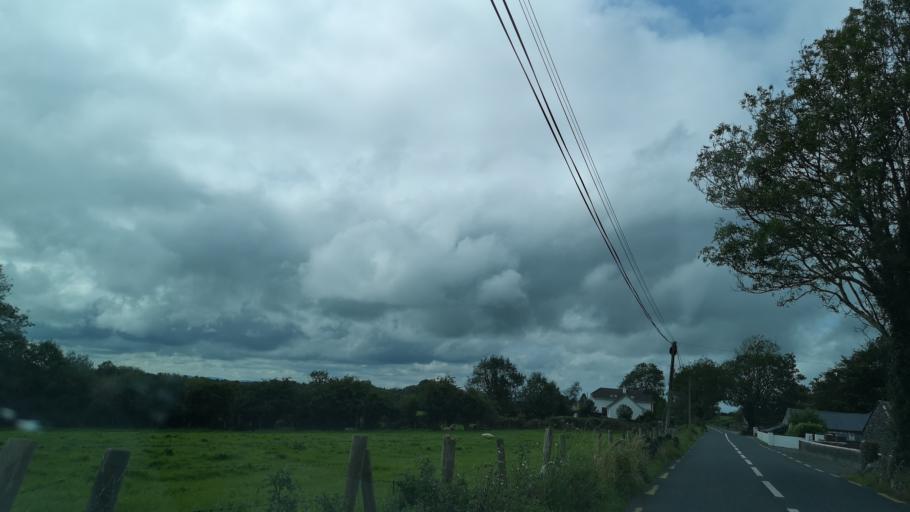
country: IE
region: Connaught
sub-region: County Galway
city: Loughrea
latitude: 53.2830
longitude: -8.6125
